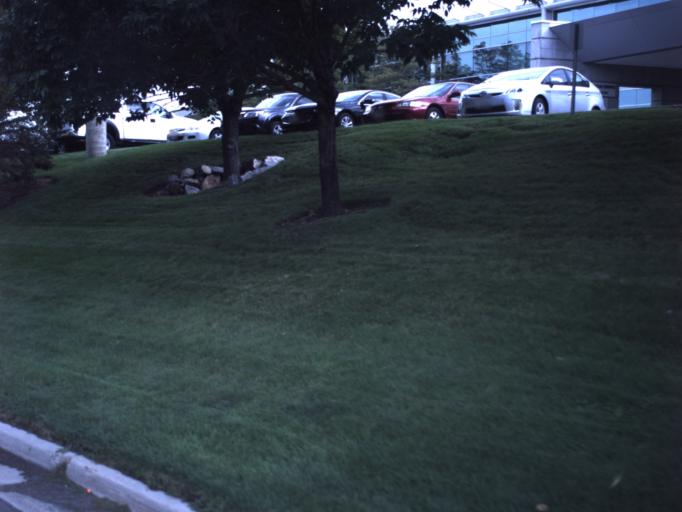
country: US
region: Utah
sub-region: Salt Lake County
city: Salt Lake City
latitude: 40.7683
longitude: -111.8366
